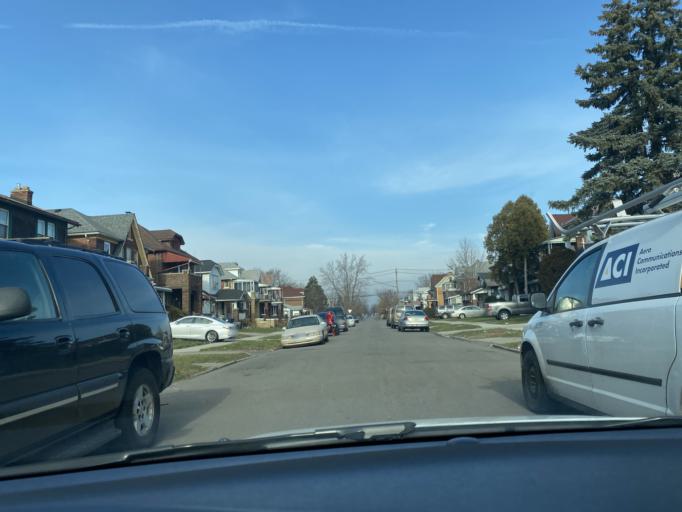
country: US
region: Michigan
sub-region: Wayne County
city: Highland Park
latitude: 42.3782
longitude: -83.1424
